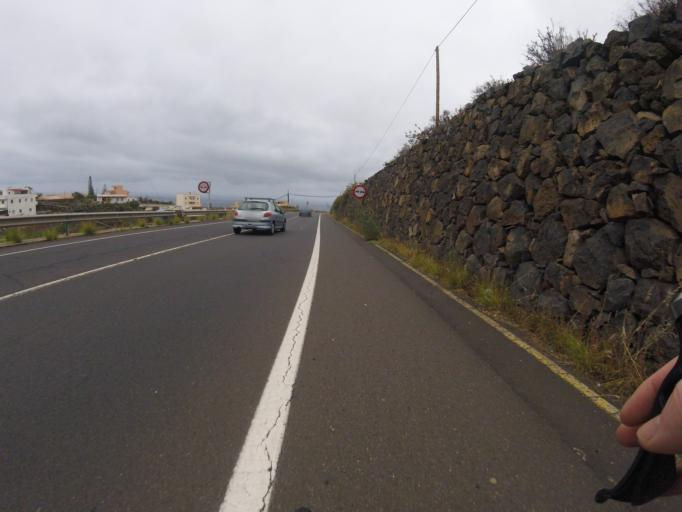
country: ES
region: Canary Islands
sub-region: Provincia de Santa Cruz de Tenerife
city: Tegueste
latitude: 28.5377
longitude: -16.3585
